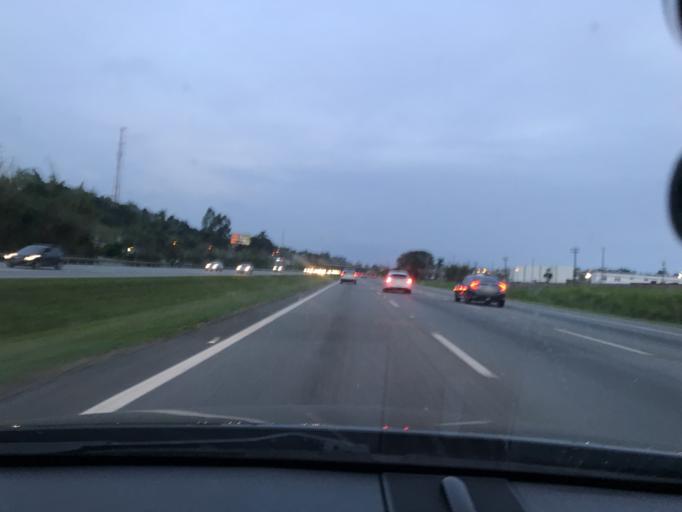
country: BR
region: Sao Paulo
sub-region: Aruja
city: Aruja
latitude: -23.4450
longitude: -46.3146
